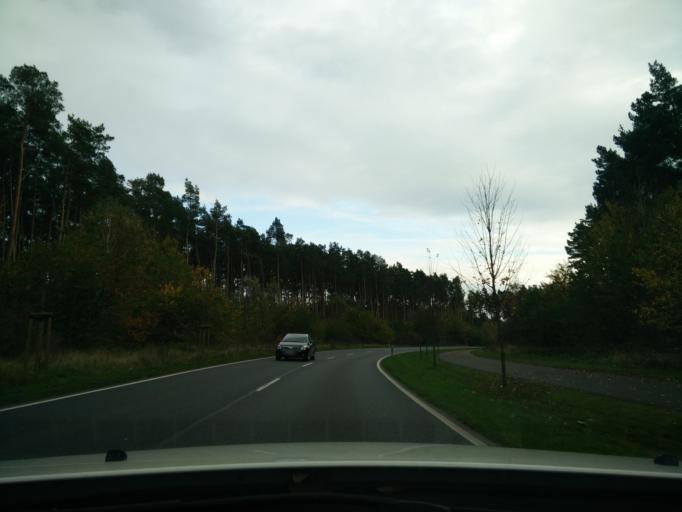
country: DE
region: Brandenburg
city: Velten
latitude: 52.6732
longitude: 13.2064
